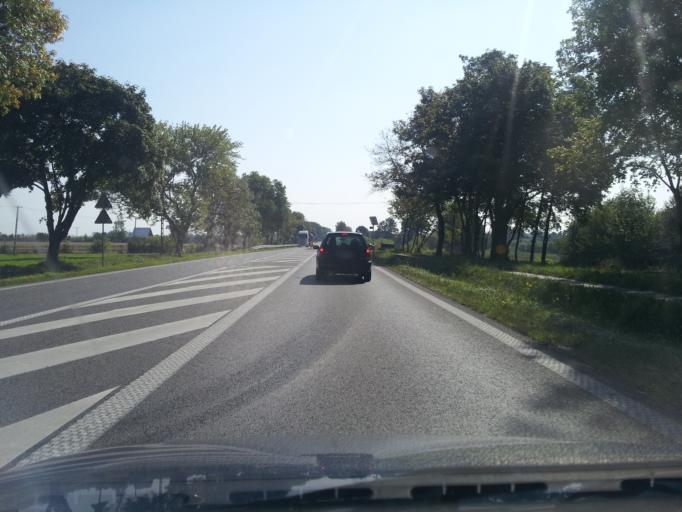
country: PL
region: Masovian Voivodeship
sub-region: Powiat sierpecki
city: Sierpc
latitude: 52.8442
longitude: 19.7180
